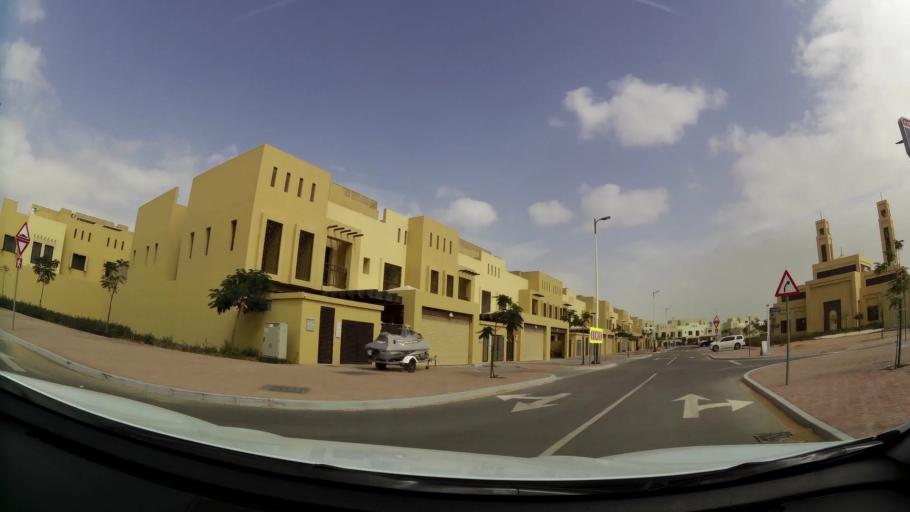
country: AE
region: Abu Dhabi
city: Abu Dhabi
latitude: 24.3991
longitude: 54.4877
